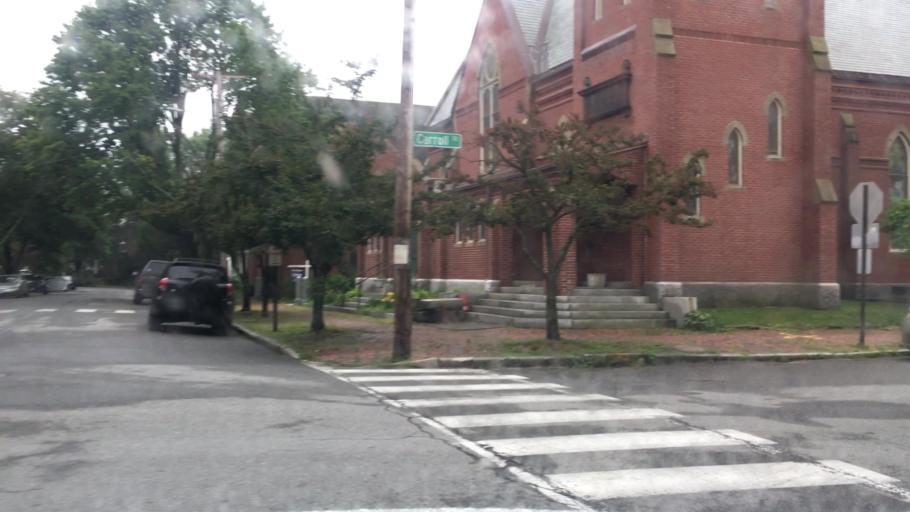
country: US
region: Maine
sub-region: Cumberland County
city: Portland
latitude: 43.6483
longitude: -70.2707
